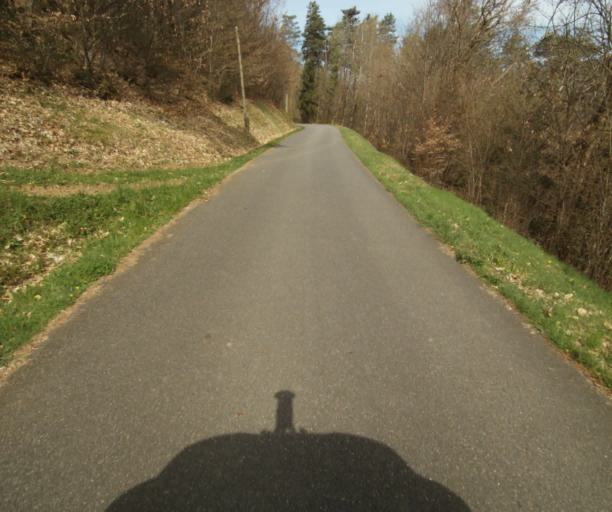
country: FR
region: Limousin
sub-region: Departement de la Correze
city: Naves
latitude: 45.3323
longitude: 1.8034
